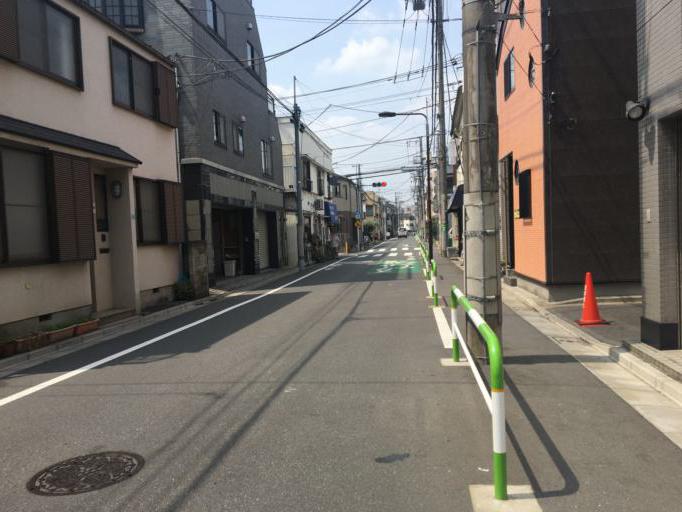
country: JP
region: Tokyo
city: Tokyo
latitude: 35.7316
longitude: 139.6931
